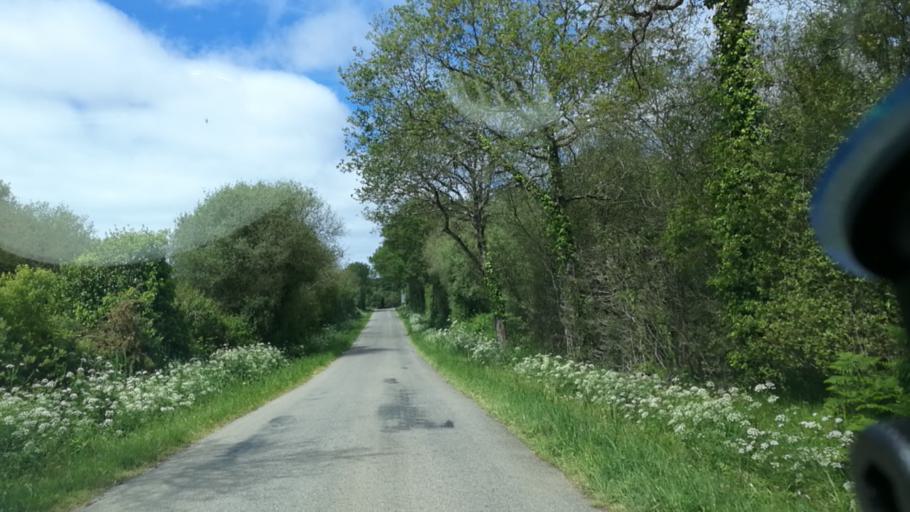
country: FR
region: Pays de la Loire
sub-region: Departement de la Loire-Atlantique
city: Asserac
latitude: 47.4458
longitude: -2.4137
